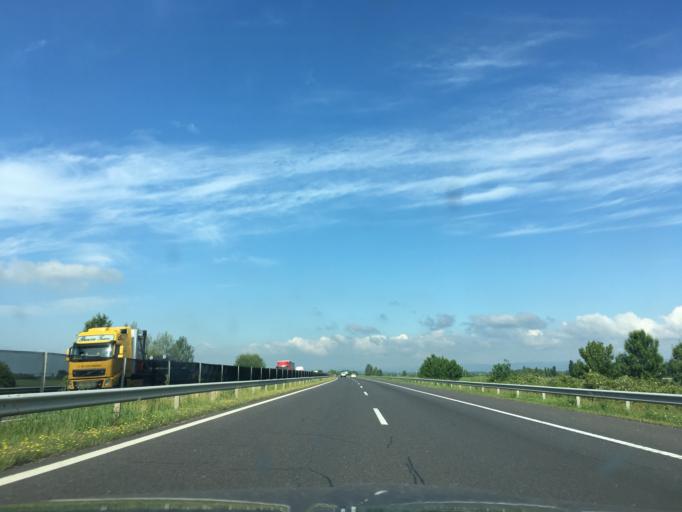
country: HU
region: Borsod-Abauj-Zemplen
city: Hejobaba
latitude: 47.8829
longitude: 20.8849
